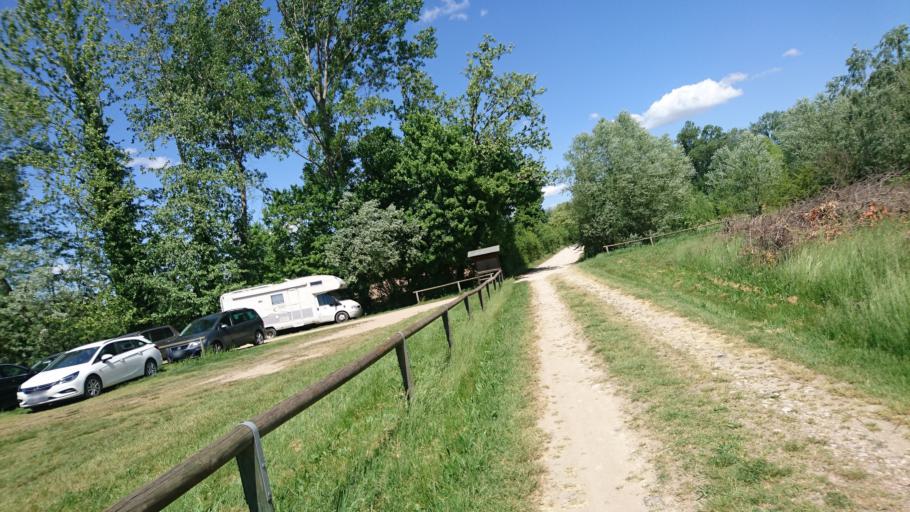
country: IT
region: Veneto
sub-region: Provincia di Treviso
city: Santa Cristina
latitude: 45.6387
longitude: 12.1276
